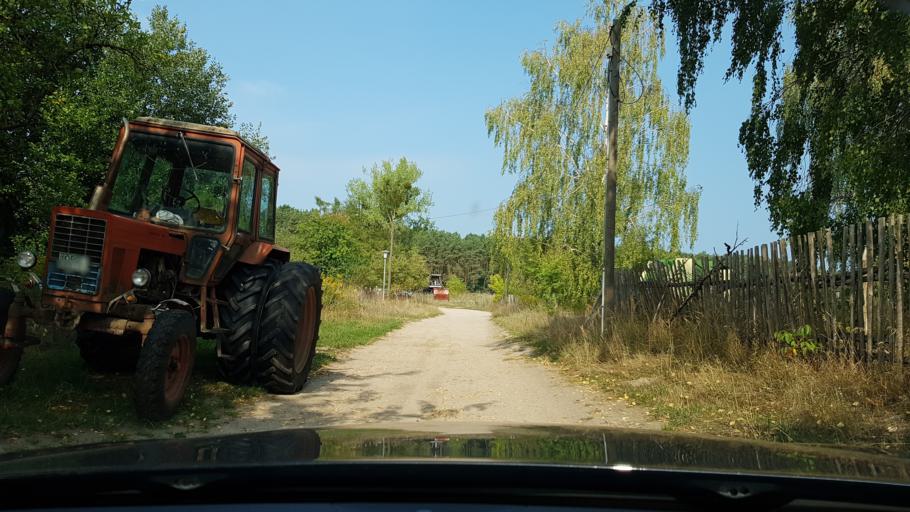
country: DE
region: Brandenburg
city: Rheinsberg
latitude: 53.0683
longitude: 12.9884
